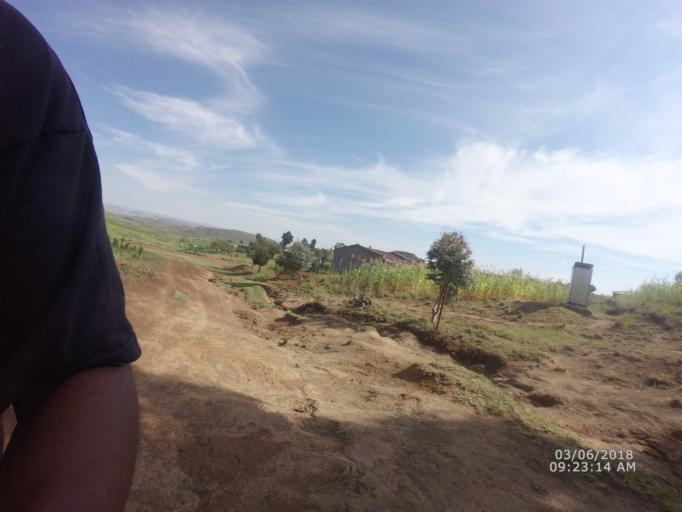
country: LS
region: Berea
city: Teyateyaneng
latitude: -29.2299
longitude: 27.8660
